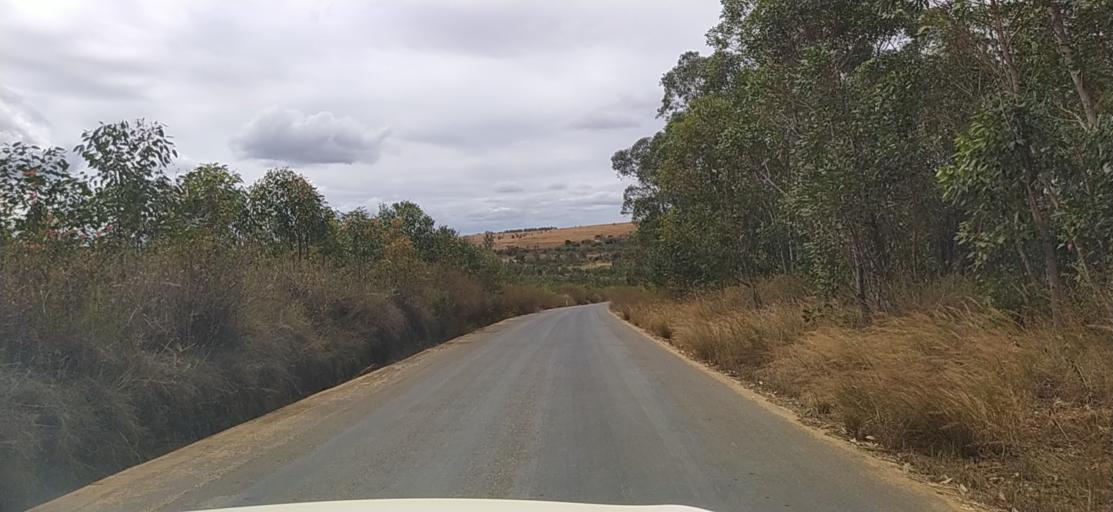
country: MG
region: Alaotra Mangoro
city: Ambatondrazaka
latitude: -17.9332
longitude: 48.2520
